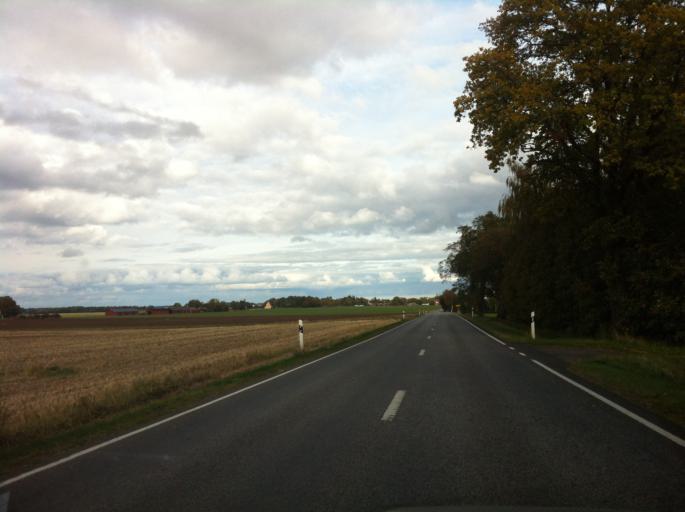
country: SE
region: OEstergoetland
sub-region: Vadstena Kommun
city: Herrestad
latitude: 58.3703
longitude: 14.7305
